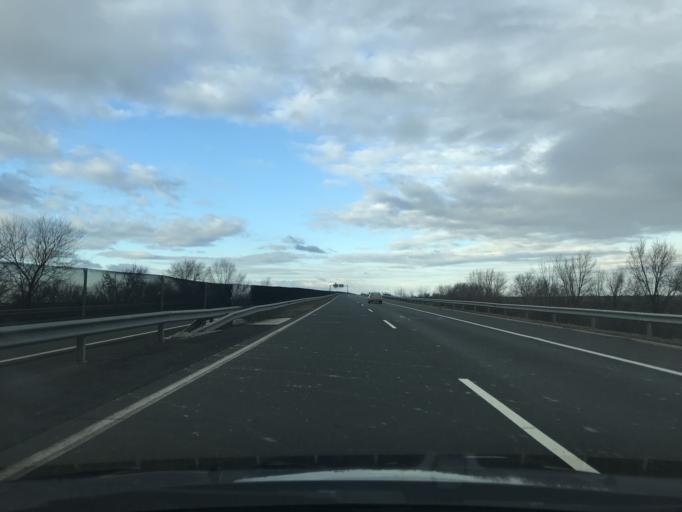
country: HU
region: Fejer
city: dunaujvaros
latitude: 46.9350
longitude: 18.8952
